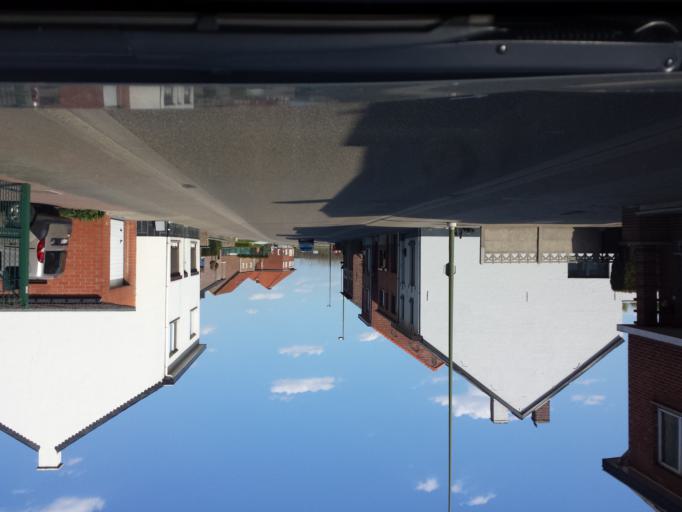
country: BE
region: Flanders
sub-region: Provincie Limburg
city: Halen
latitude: 50.9500
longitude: 5.1162
